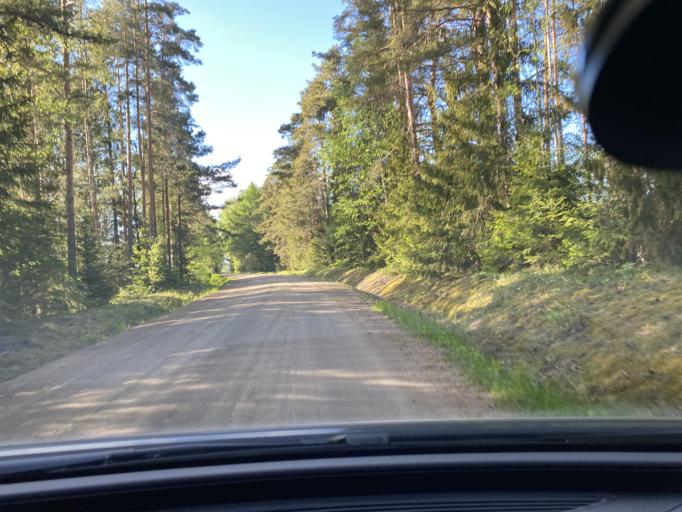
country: FI
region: Satakunta
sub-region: Pori
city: Huittinen
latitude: 61.1383
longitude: 22.8333
